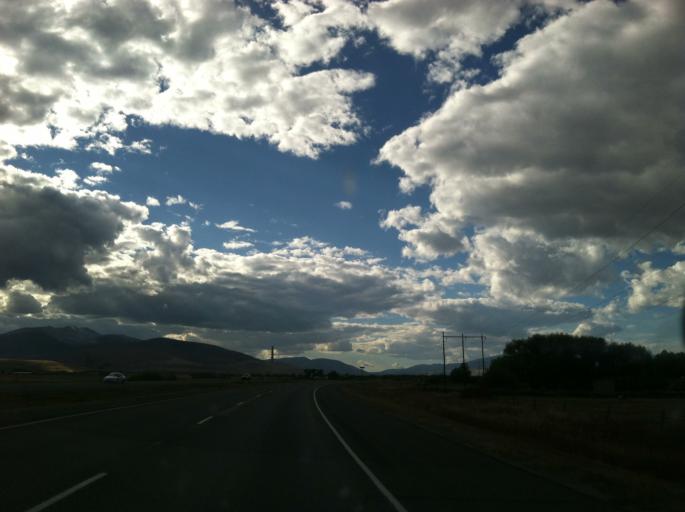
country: US
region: Montana
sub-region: Deer Lodge County
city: Warm Springs
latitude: 46.0963
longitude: -112.8243
